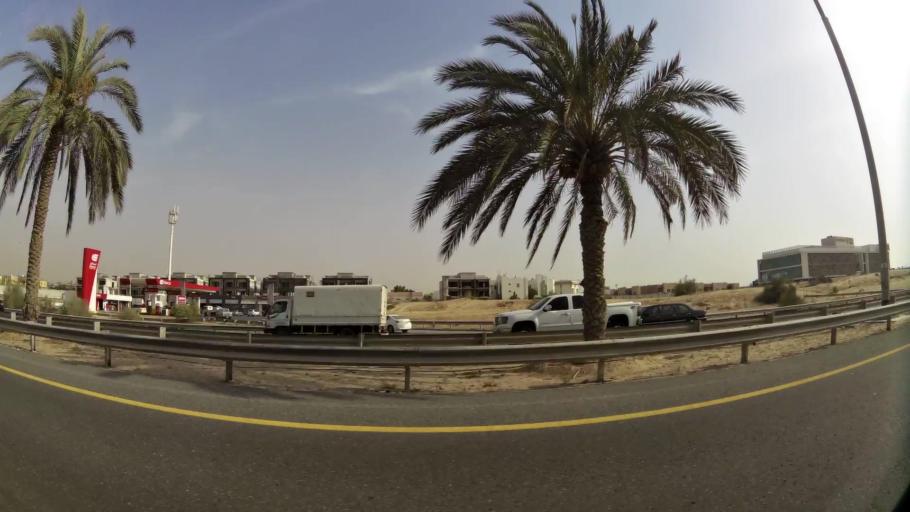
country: AE
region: Ash Shariqah
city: Sharjah
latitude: 25.2334
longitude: 55.4348
